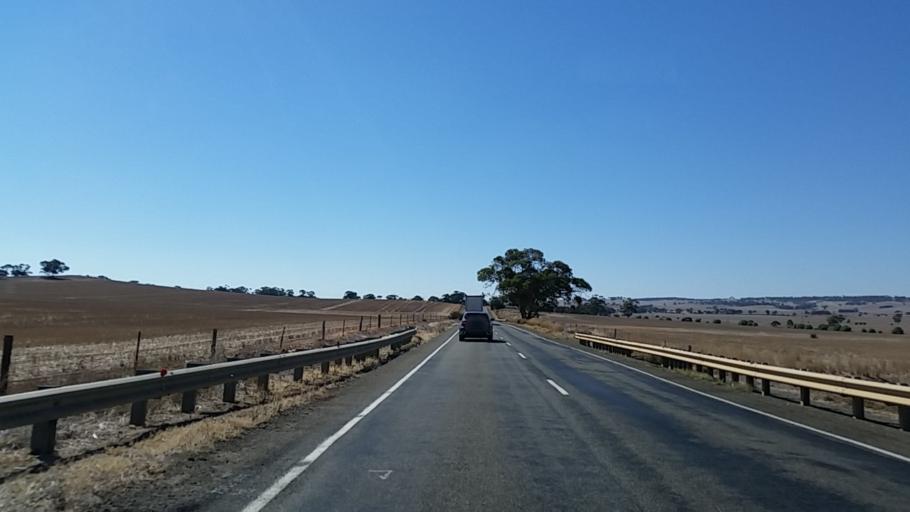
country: AU
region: South Australia
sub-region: Clare and Gilbert Valleys
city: Clare
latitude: -34.0202
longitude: 138.8078
